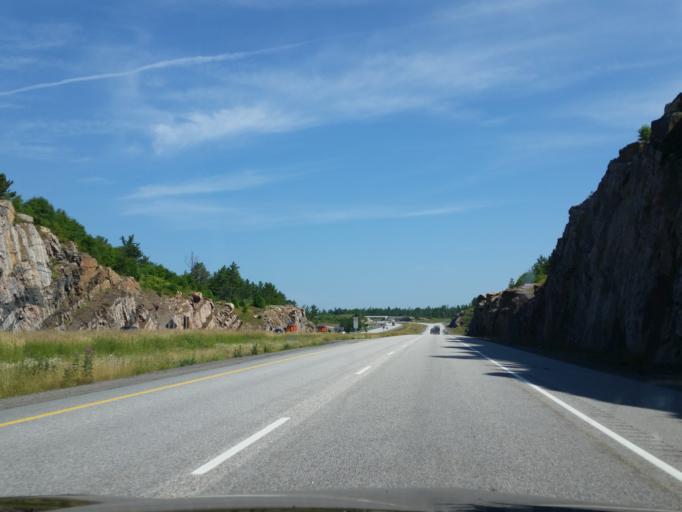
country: CA
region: Ontario
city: Greater Sudbury
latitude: 46.2170
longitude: -80.7697
